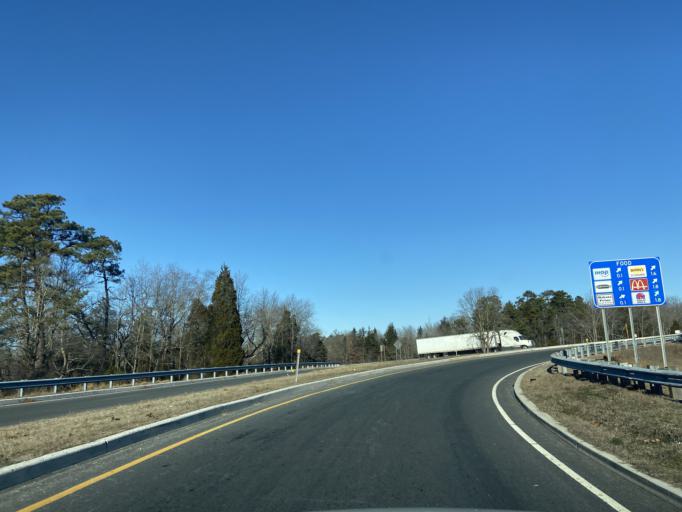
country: US
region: New Jersey
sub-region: Cumberland County
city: Vineland
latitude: 39.4875
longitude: -75.0729
